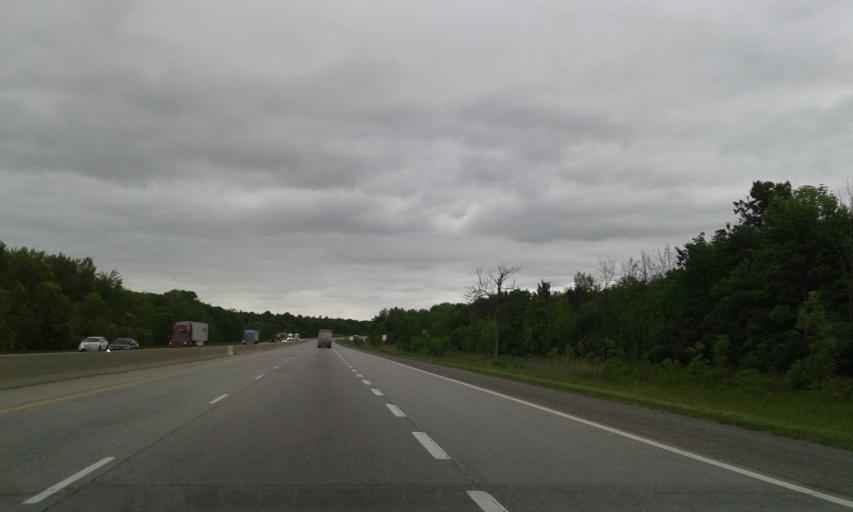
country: CA
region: Ontario
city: Brockville
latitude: 44.5356
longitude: -75.7676
